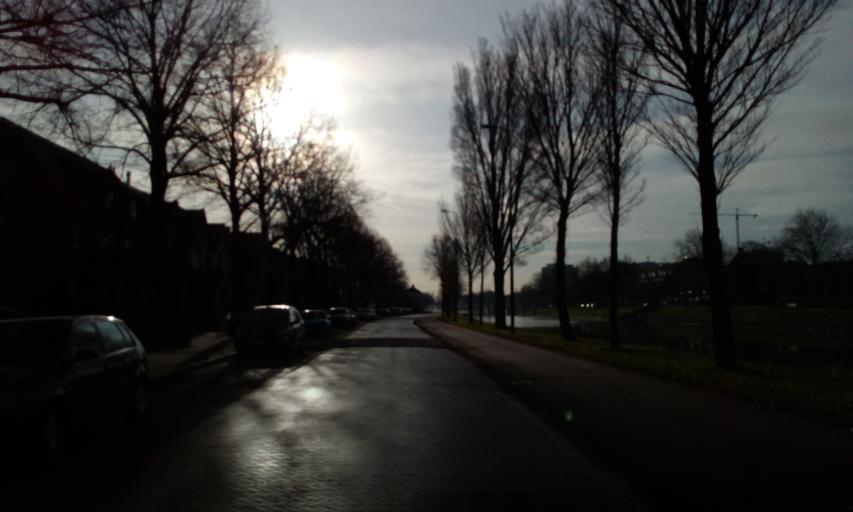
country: NL
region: South Holland
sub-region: Gemeente Rijswijk
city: Rijswijk
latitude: 52.0494
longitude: 4.3434
